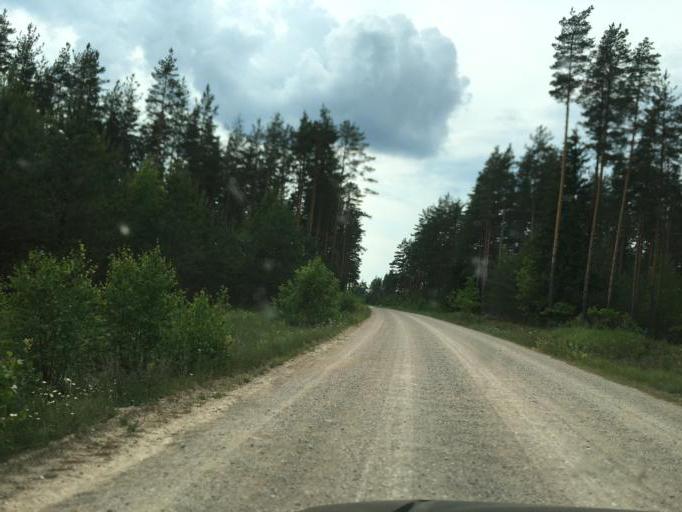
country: LV
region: Rugaju
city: Rugaji
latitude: 56.7522
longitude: 27.0823
